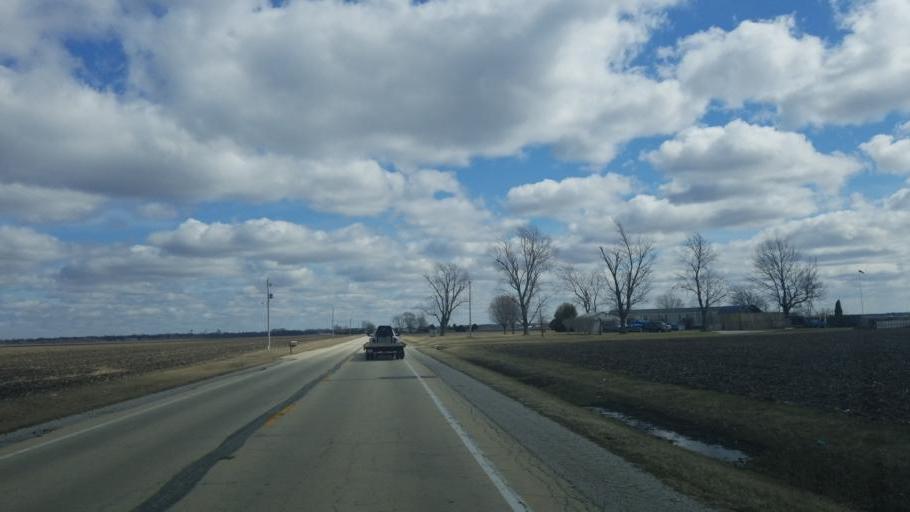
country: US
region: Illinois
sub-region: Douglas County
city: Atwood
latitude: 39.7920
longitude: -88.5034
